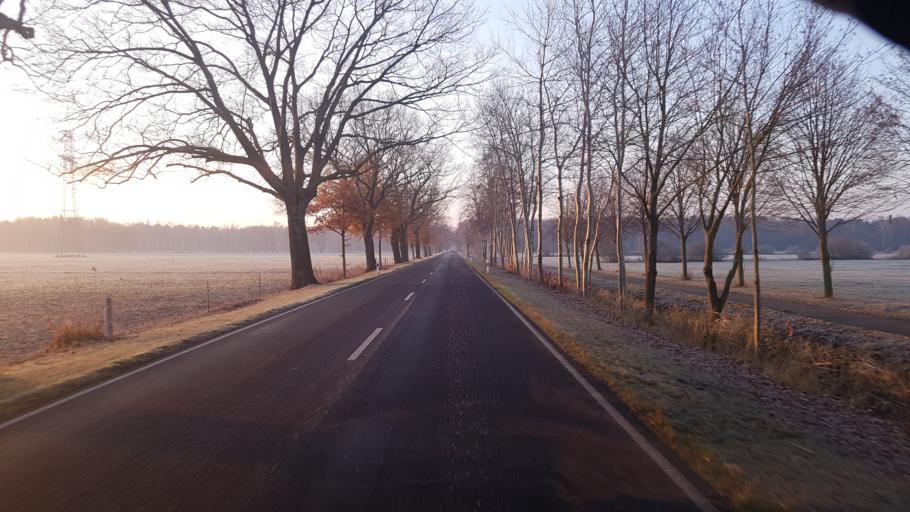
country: DE
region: Brandenburg
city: Tettau
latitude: 51.4528
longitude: 13.7386
